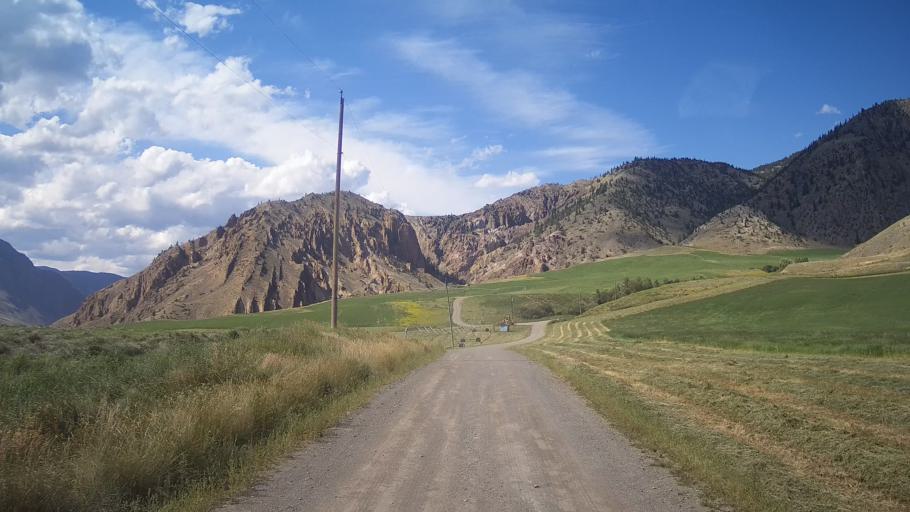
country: CA
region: British Columbia
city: Lillooet
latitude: 51.1859
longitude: -122.1181
